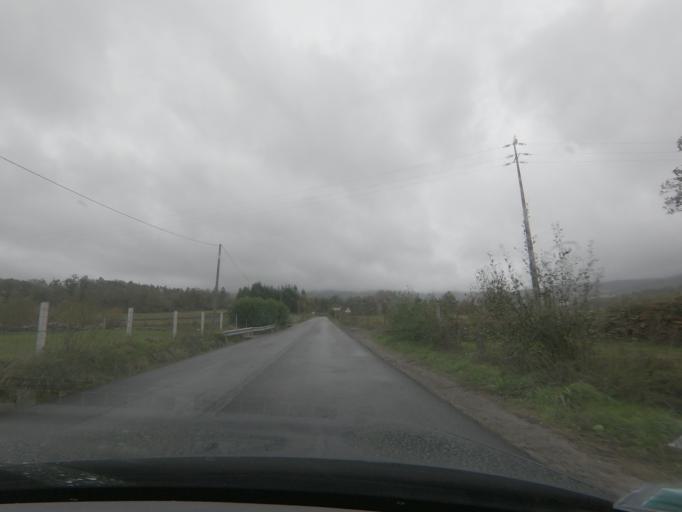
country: PT
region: Vila Real
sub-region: Santa Marta de Penaguiao
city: Santa Marta de Penaguiao
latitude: 41.2861
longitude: -7.8629
